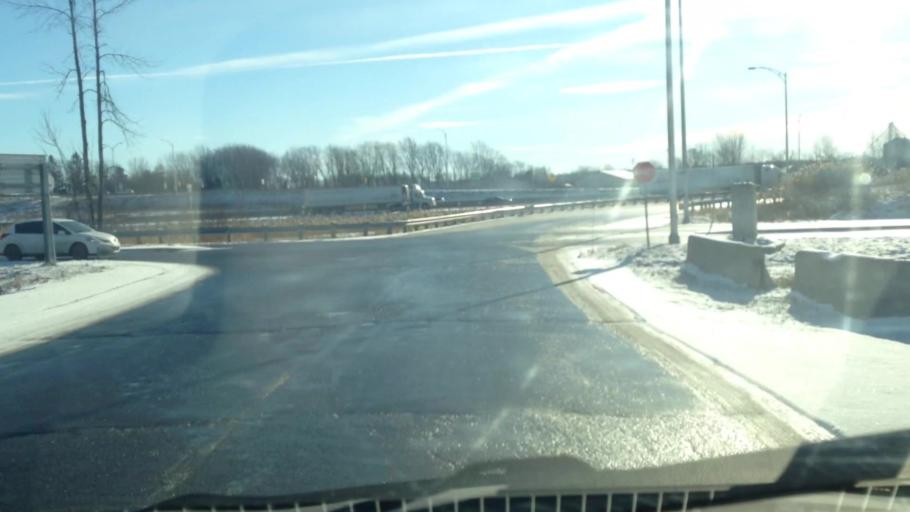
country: CA
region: Quebec
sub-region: Monteregie
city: Mercier
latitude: 45.3423
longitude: -73.7613
